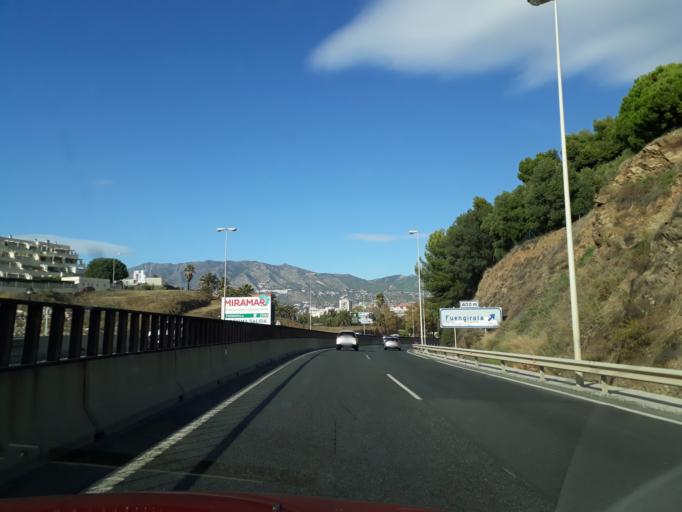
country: ES
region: Andalusia
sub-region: Provincia de Malaga
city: Fuengirola
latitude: 36.5247
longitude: -4.6302
